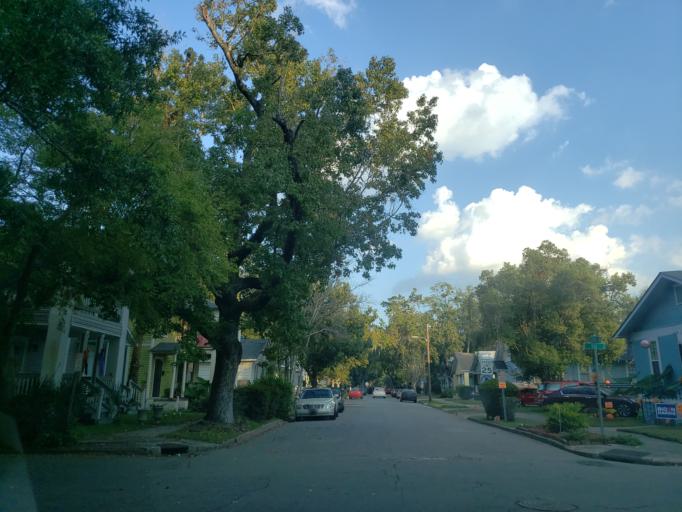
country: US
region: Georgia
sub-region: Chatham County
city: Savannah
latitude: 32.0562
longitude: -81.0839
